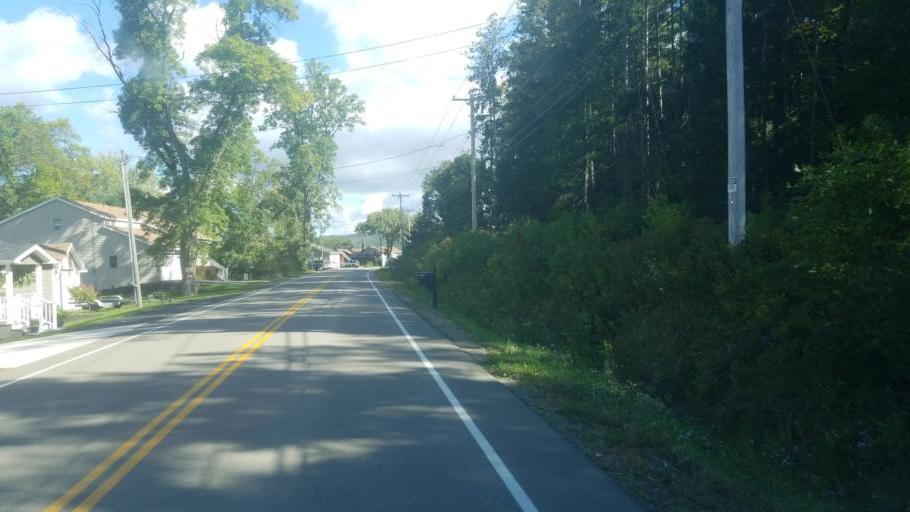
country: US
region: New York
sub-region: Allegany County
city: Cuba
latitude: 42.2399
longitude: -78.3049
